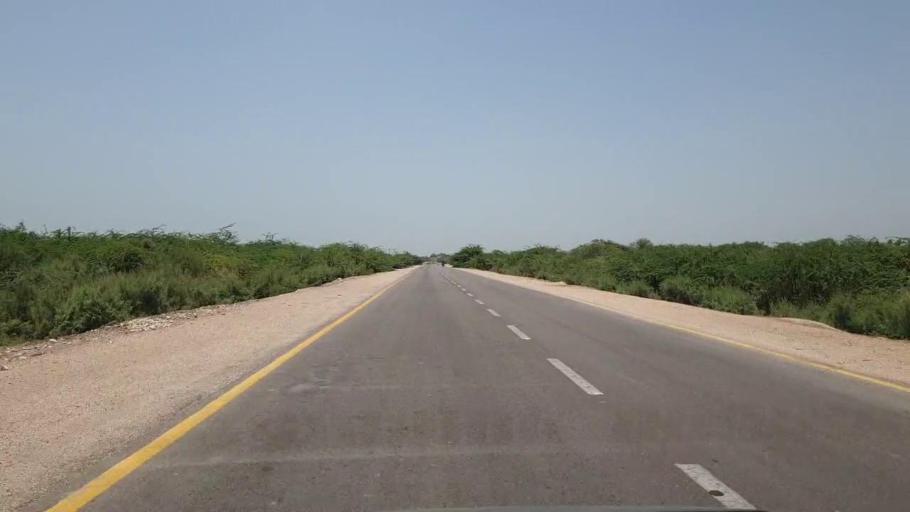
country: PK
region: Sindh
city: Sakrand
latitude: 26.1169
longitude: 68.3860
